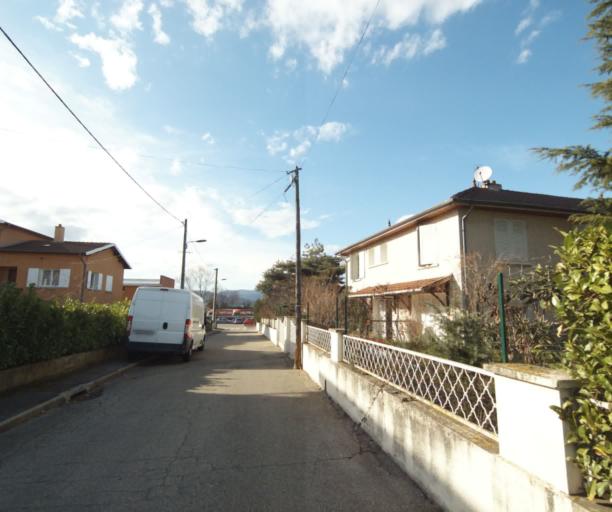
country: FR
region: Rhone-Alpes
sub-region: Departement de l'Ardeche
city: Davezieux
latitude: 45.2568
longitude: 4.6978
